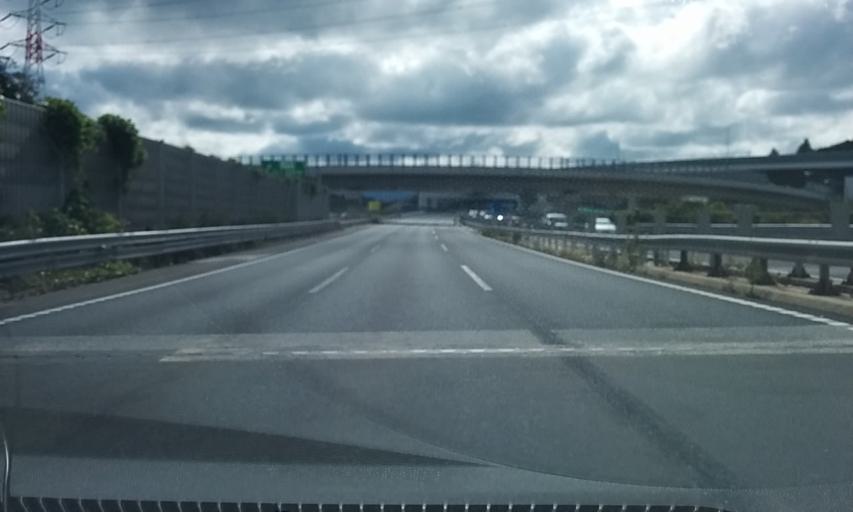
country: JP
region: Hyogo
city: Sandacho
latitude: 34.8514
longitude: 135.2212
